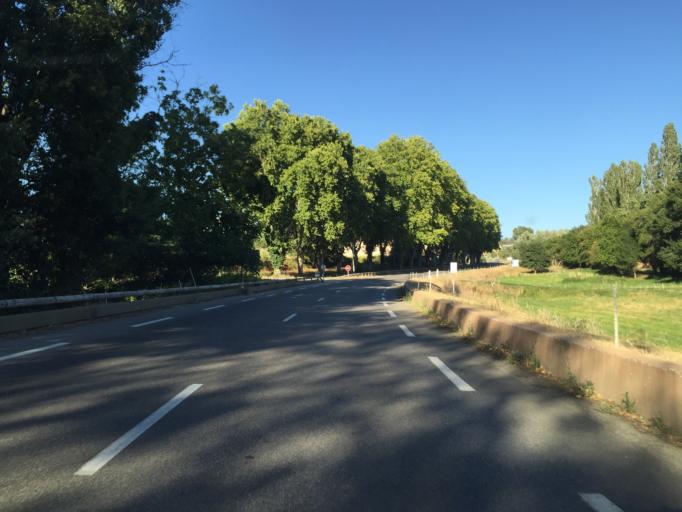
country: FR
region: Provence-Alpes-Cote d'Azur
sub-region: Departement des Alpes-de-Haute-Provence
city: Reillanne
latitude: 43.8625
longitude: 5.6575
